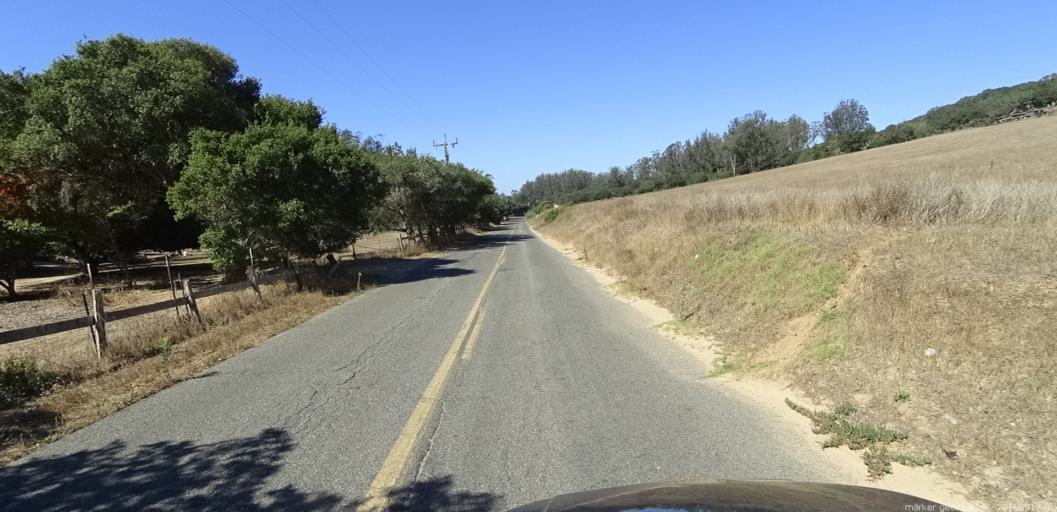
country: US
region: California
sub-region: Monterey County
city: Elkhorn
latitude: 36.8259
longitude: -121.7119
